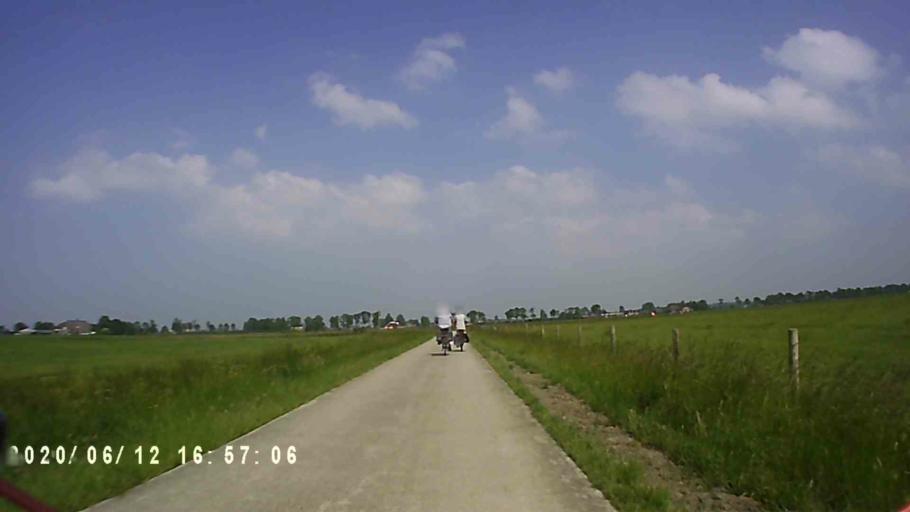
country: NL
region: Groningen
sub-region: Gemeente Groningen
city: Korrewegwijk
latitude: 53.2651
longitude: 6.5570
